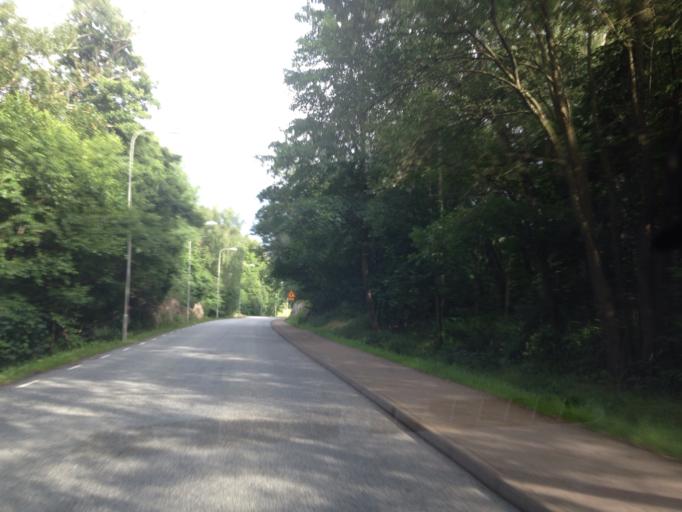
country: SE
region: Vaestra Goetaland
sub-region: Goteborg
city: Goeteborg
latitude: 57.7601
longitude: 11.9827
